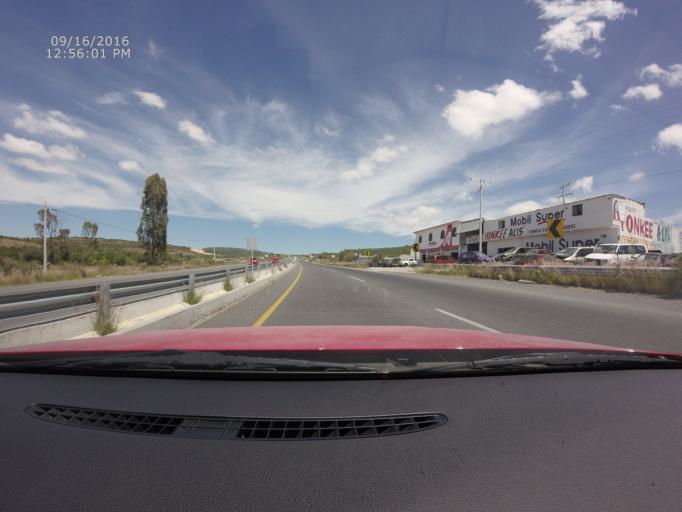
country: MX
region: Queretaro
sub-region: Colon
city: Purisima de Cubos (La Purisima)
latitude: 20.6470
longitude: -100.0990
